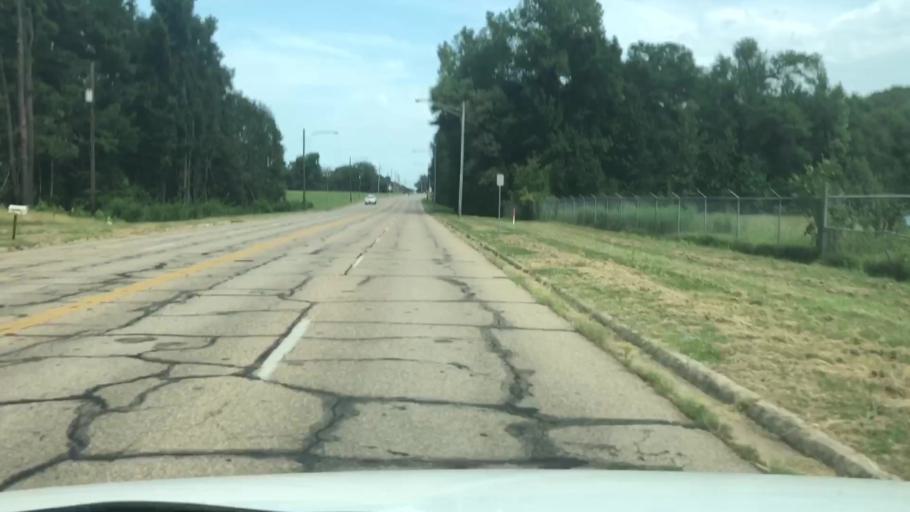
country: US
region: Texas
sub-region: Bowie County
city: Wake Village
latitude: 33.4098
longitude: -94.0803
